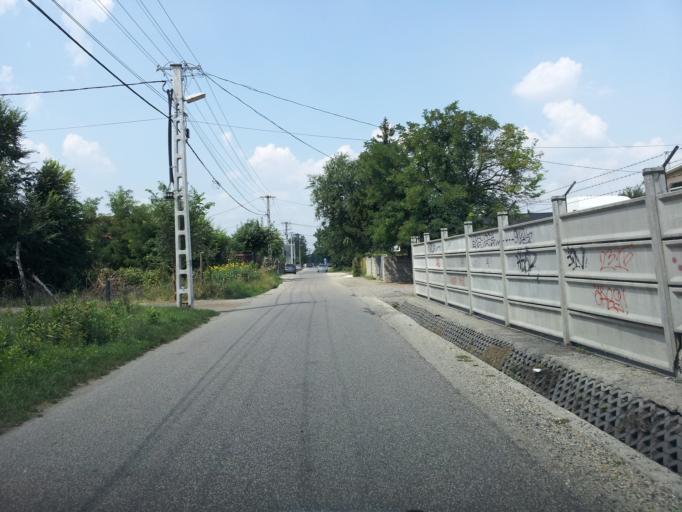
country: HU
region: Pest
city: Szigethalom
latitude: 47.3174
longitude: 19.0182
